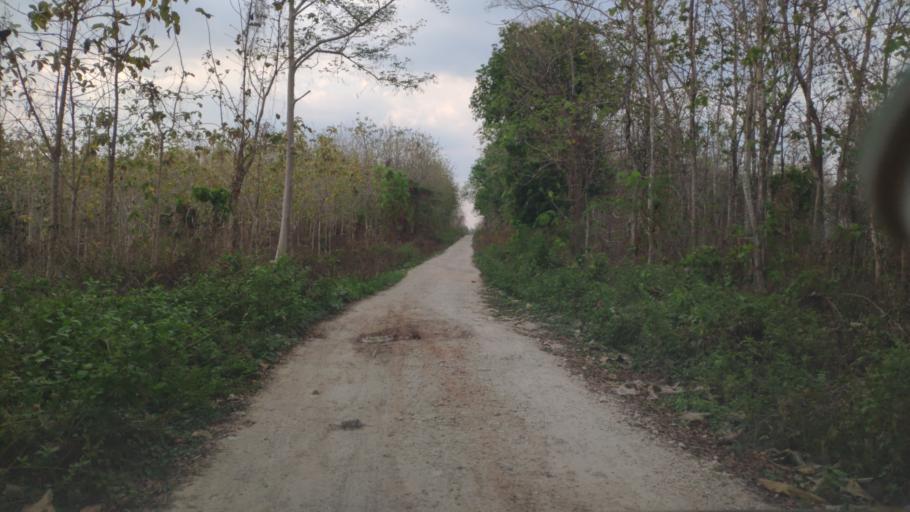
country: ID
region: Central Java
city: Randublatung
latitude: -7.2812
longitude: 111.2892
